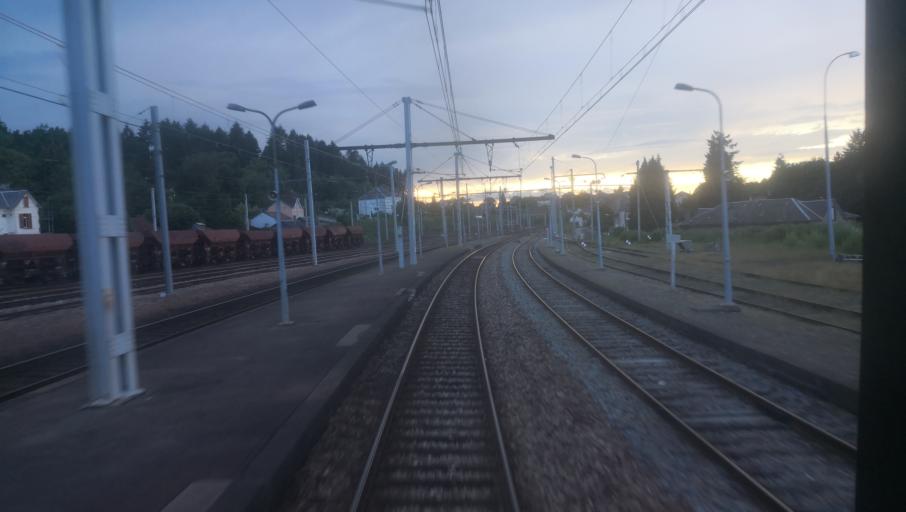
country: FR
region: Limousin
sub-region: Departement de la Haute-Vienne
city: Ambazac
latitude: 46.0474
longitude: 1.4750
